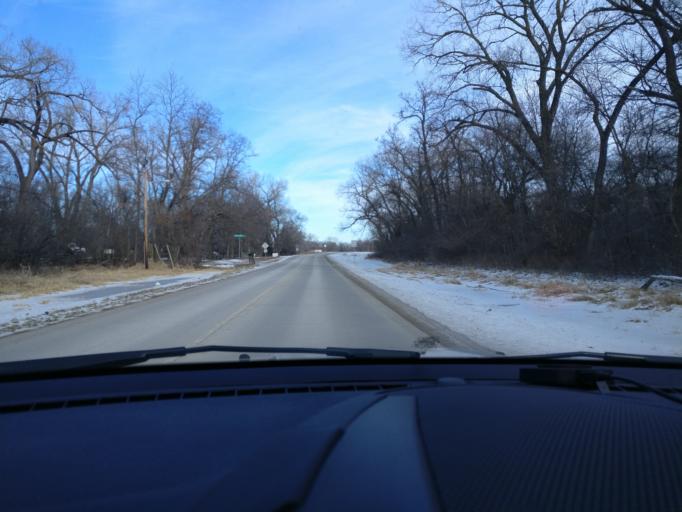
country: US
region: Nebraska
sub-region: Dodge County
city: Fremont
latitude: 41.4128
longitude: -96.5110
